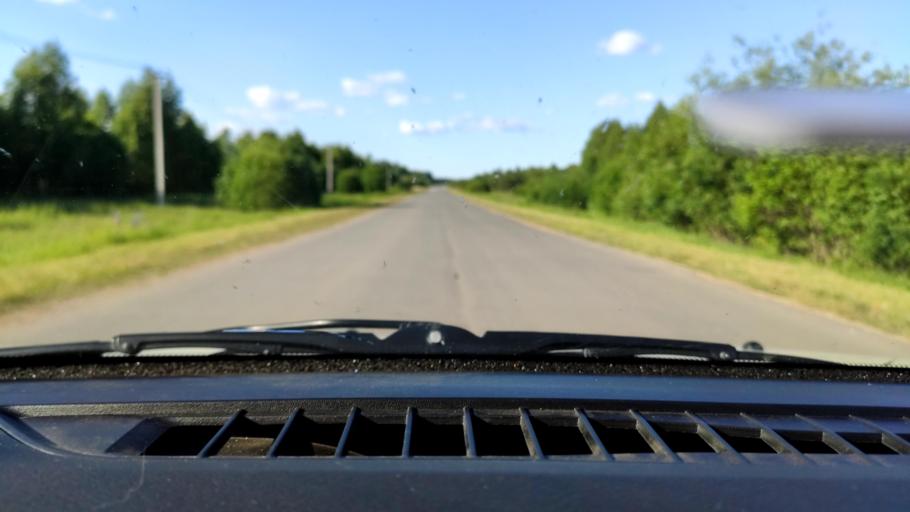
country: RU
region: Perm
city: Uinskoye
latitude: 57.1102
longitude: 56.6637
